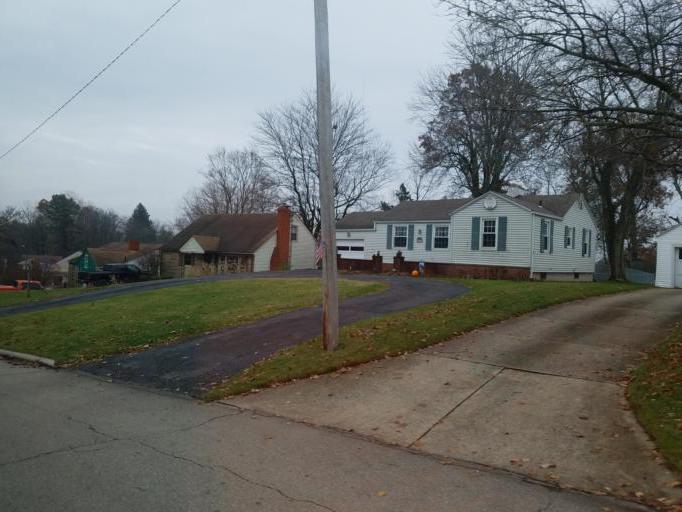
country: US
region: Ohio
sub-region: Richland County
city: Mansfield
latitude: 40.7290
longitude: -82.5398
